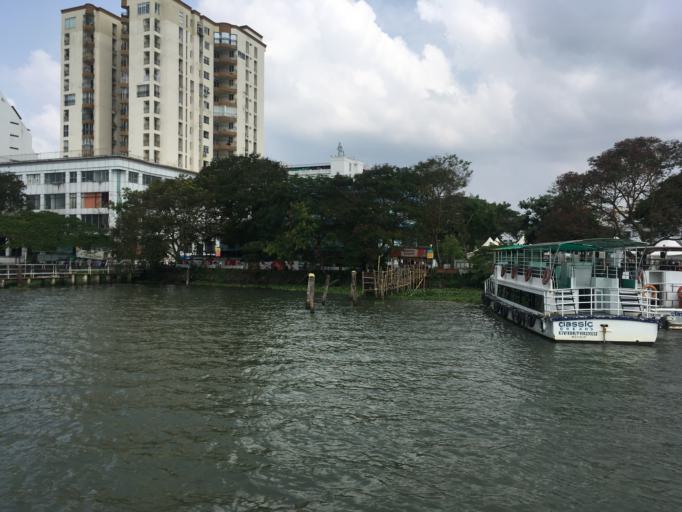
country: IN
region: Kerala
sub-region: Ernakulam
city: Cochin
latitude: 9.9821
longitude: 76.2733
